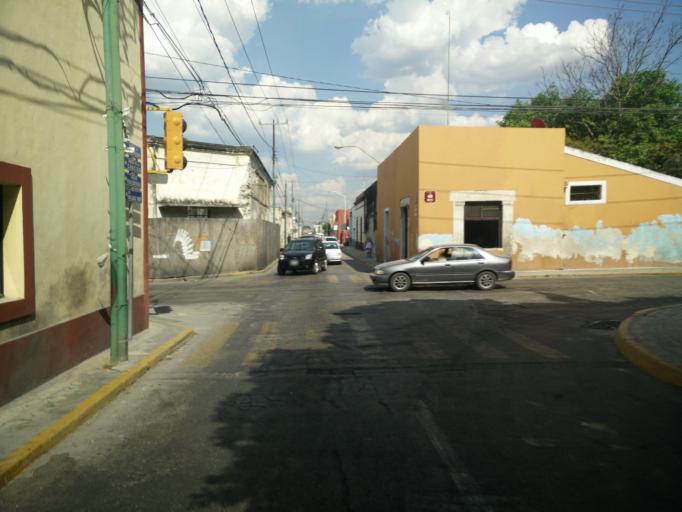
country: MX
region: Yucatan
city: Merida
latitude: 20.9687
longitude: -89.6148
